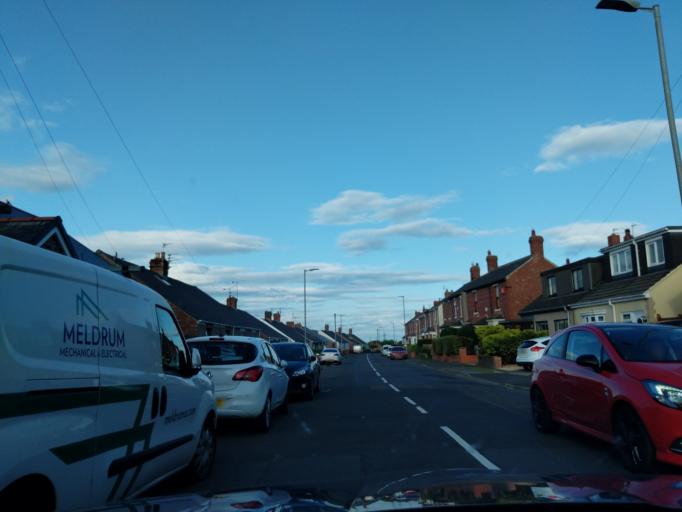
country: GB
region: England
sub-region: Northumberland
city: Bedlington
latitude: 55.1328
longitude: -1.5746
